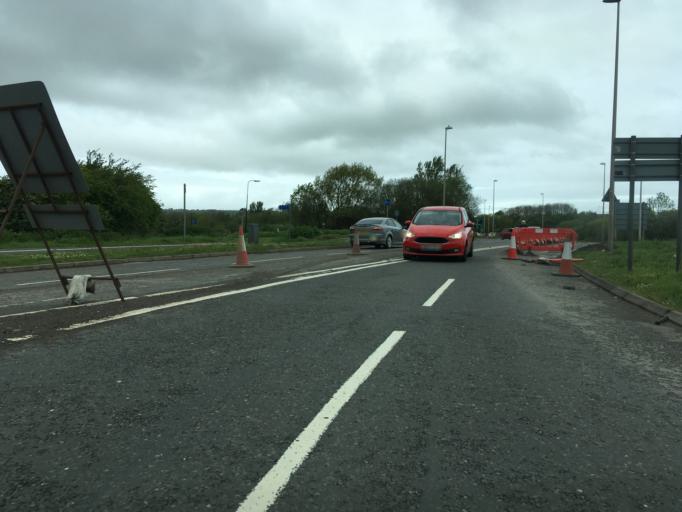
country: GB
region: England
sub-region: North Somerset
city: Hutton
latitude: 51.3422
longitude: -2.9318
